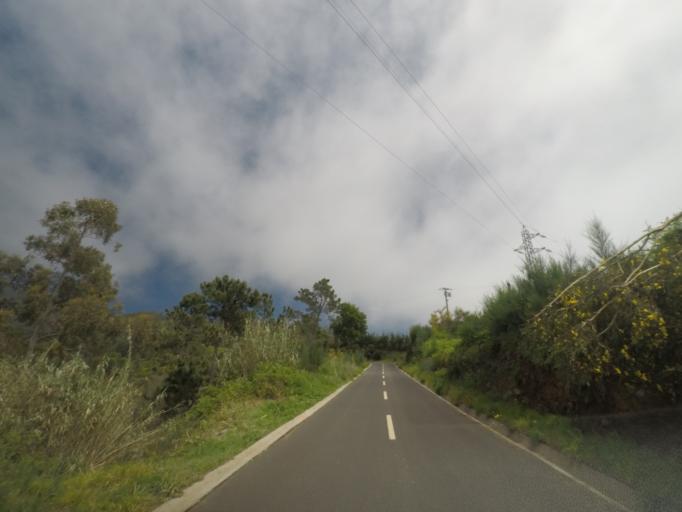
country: PT
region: Madeira
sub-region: Calheta
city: Arco da Calheta
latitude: 32.7221
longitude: -17.1221
